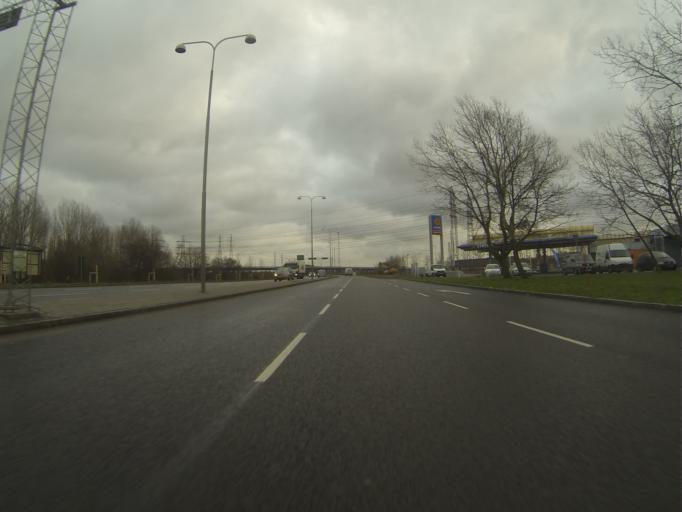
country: SE
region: Skane
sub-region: Burlovs Kommun
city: Arloev
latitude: 55.6287
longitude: 13.0472
